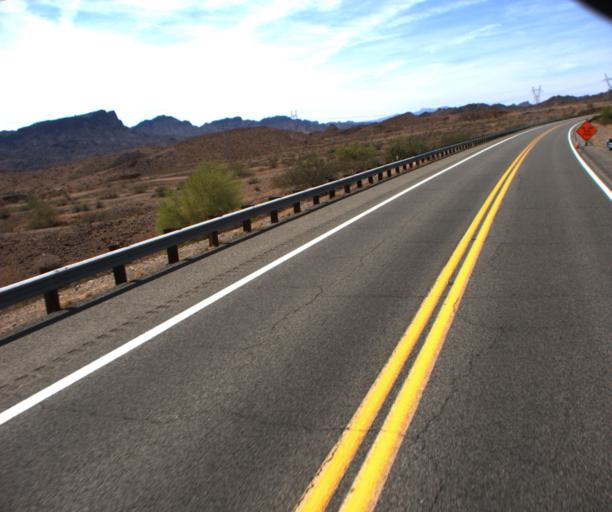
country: US
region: Arizona
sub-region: La Paz County
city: Cienega Springs
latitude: 34.3269
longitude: -114.1308
